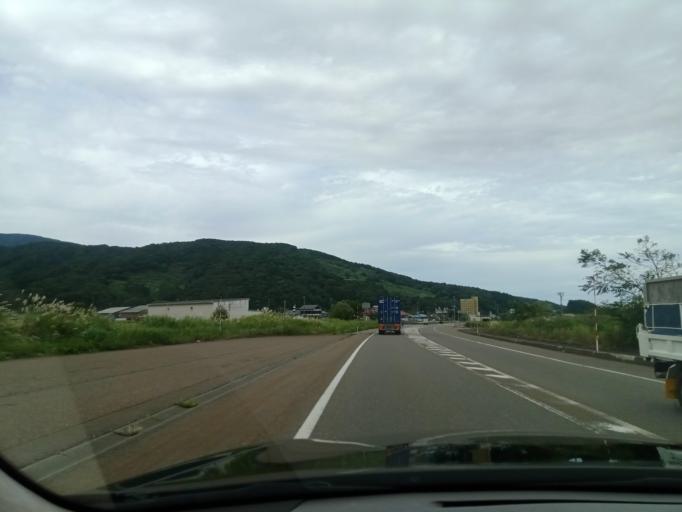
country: JP
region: Niigata
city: Arai
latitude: 37.0222
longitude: 138.2271
